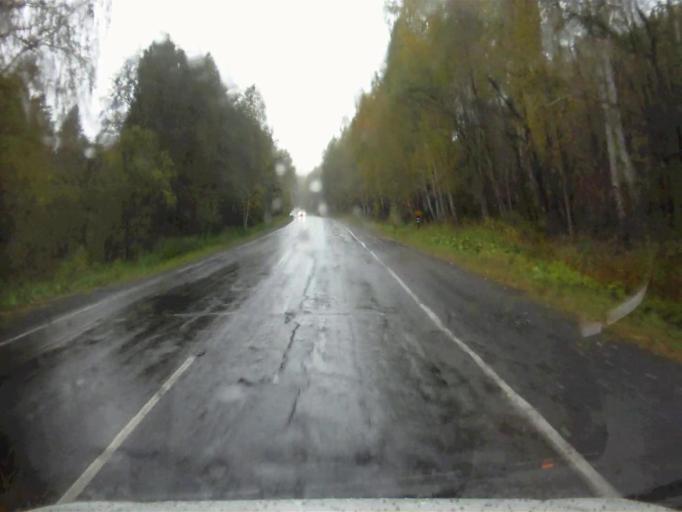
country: RU
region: Chelyabinsk
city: Kyshtym
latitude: 55.9088
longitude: 60.4376
